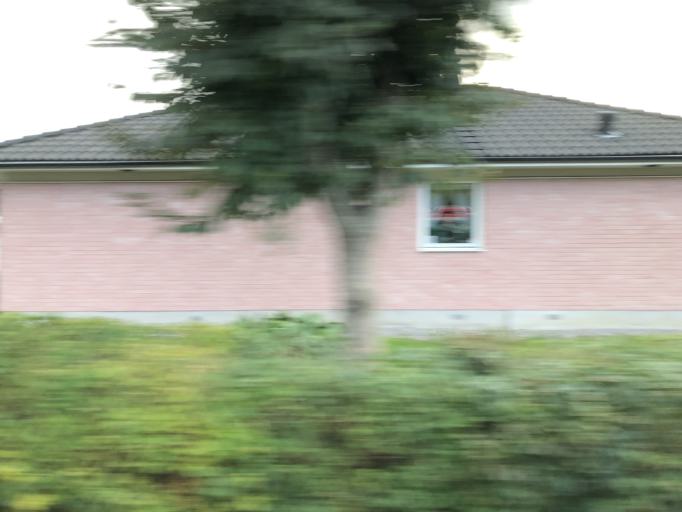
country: SE
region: Stockholm
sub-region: Jarfalla Kommun
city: Jakobsberg
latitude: 59.4277
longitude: 17.8218
